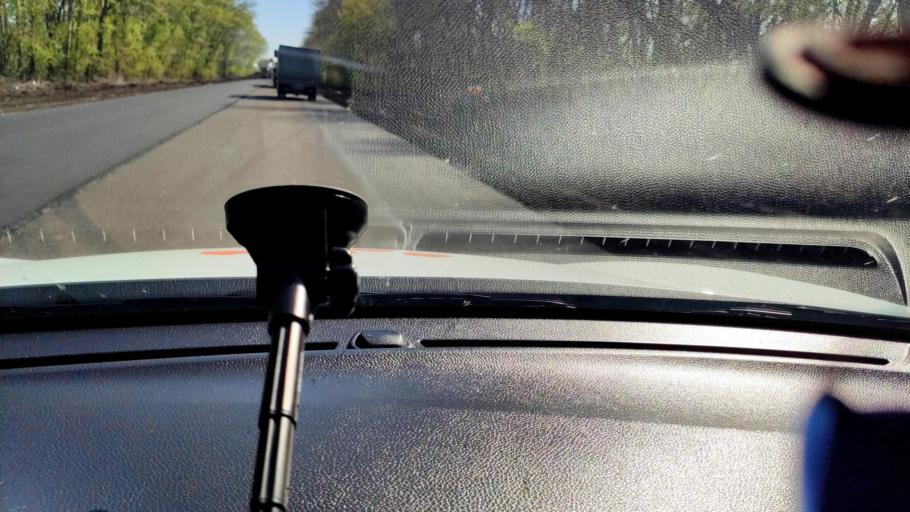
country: RU
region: Voronezj
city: Uryv-Pokrovka
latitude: 51.1776
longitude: 39.0796
